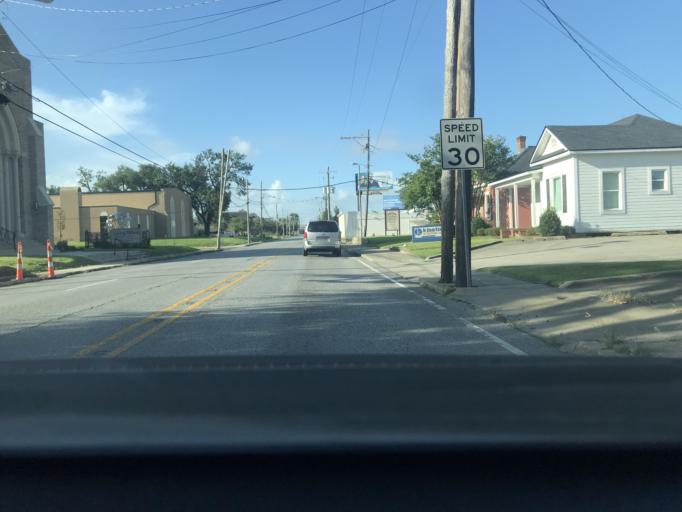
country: US
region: Louisiana
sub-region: Calcasieu Parish
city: Lake Charles
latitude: 30.2179
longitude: -93.2192
